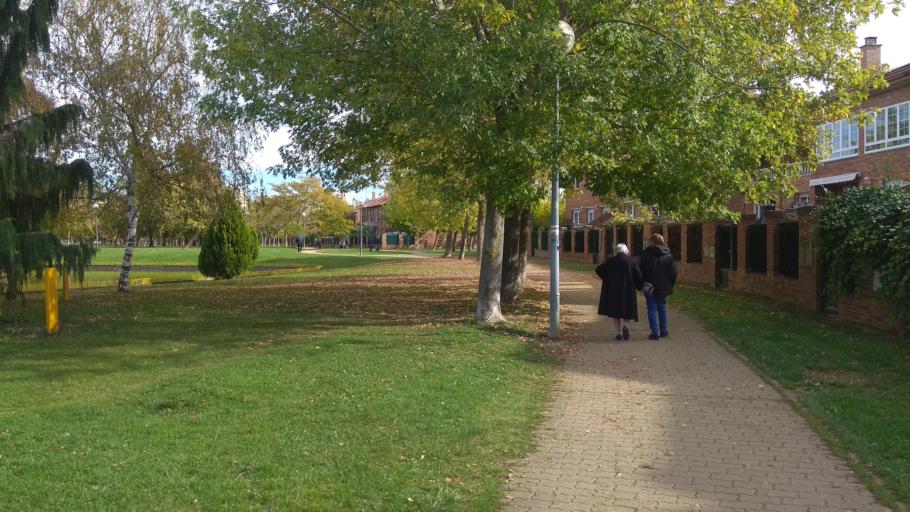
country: ES
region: Navarre
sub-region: Provincia de Navarra
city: Cizur Mayor
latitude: 42.8021
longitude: -1.6917
